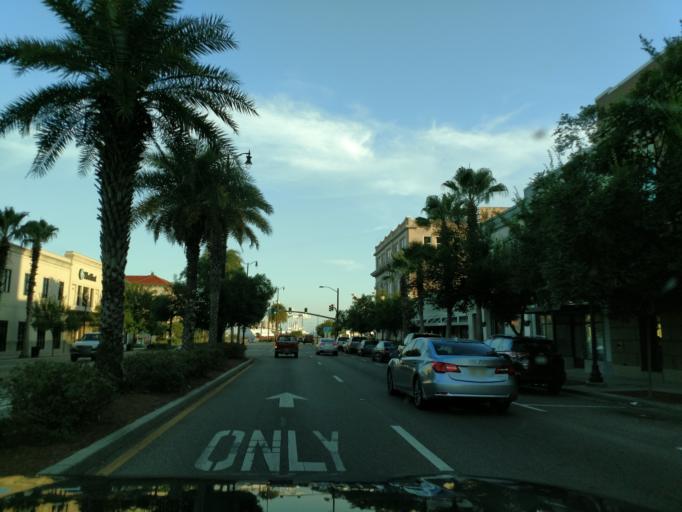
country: US
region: Mississippi
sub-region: Harrison County
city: Gulfport
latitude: 30.3681
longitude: -89.0930
